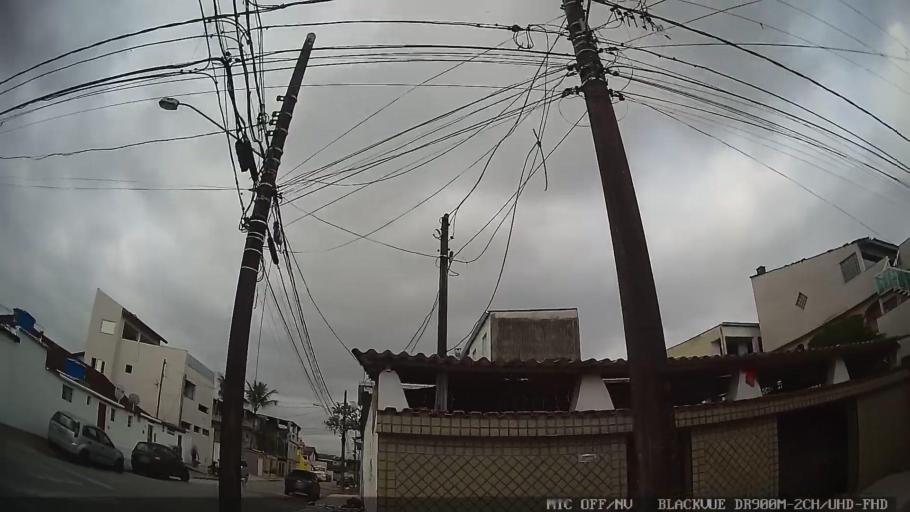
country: BR
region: Sao Paulo
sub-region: Santos
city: Santos
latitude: -23.9443
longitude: -46.2897
